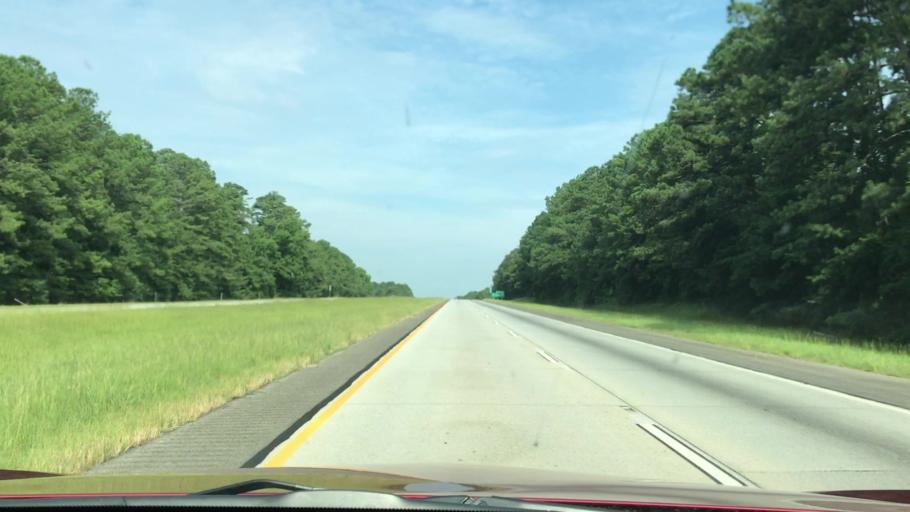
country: US
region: Georgia
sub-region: Warren County
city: Firing Range
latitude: 33.5004
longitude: -82.7041
